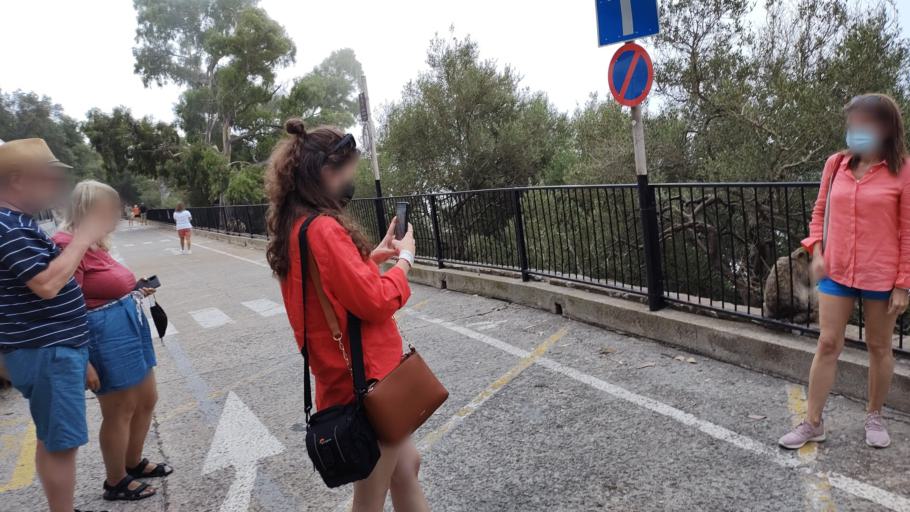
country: GI
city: Gibraltar
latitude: 36.1266
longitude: -5.3458
